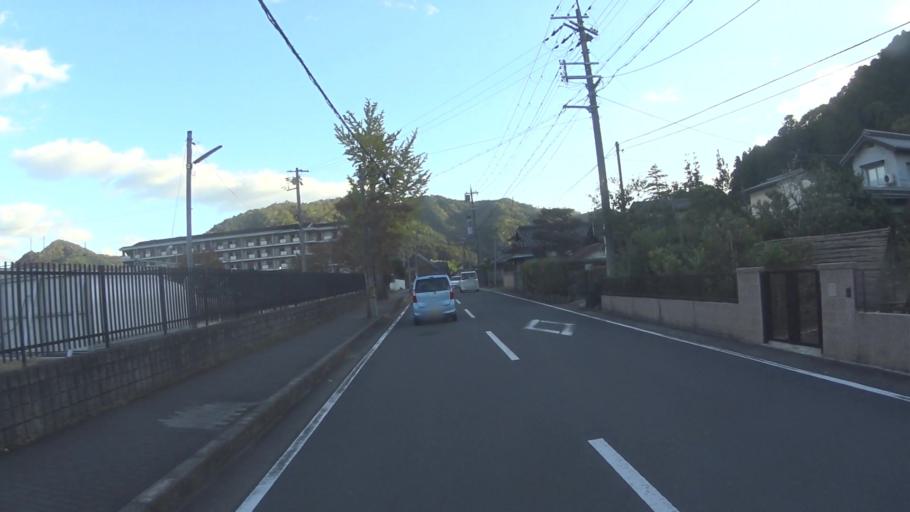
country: JP
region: Kyoto
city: Ayabe
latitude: 35.2937
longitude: 135.2578
